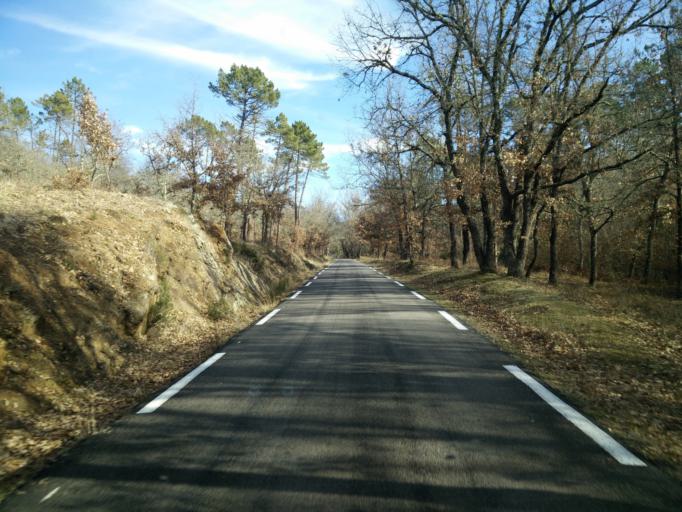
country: FR
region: Provence-Alpes-Cote d'Azur
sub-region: Departement du Var
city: Saint-Paul-en-Foret
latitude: 43.5702
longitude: 6.6644
